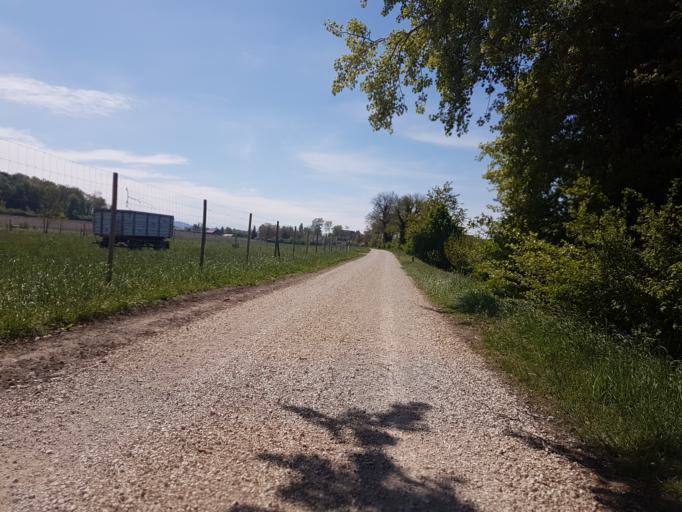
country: CH
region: Neuchatel
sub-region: Neuchatel District
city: Cornaux
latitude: 47.0278
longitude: 7.0338
